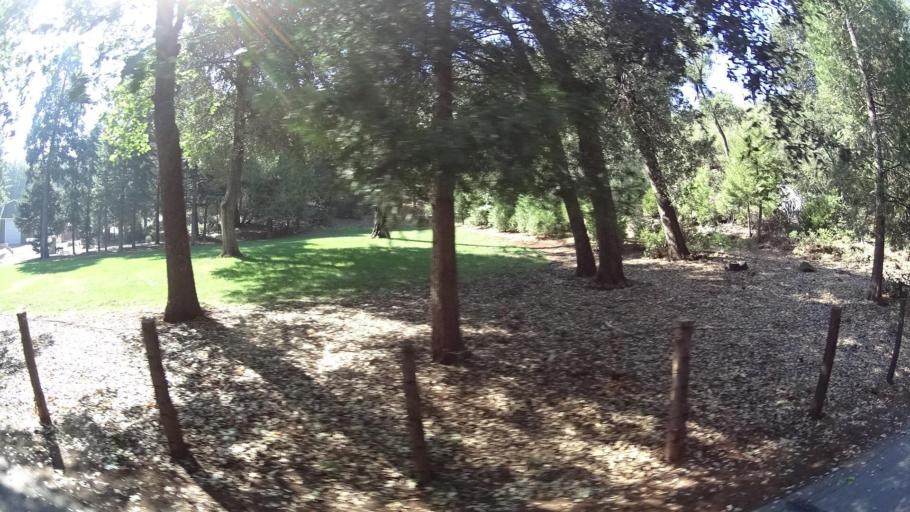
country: US
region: California
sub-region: San Diego County
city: Julian
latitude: 33.0211
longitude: -116.5810
